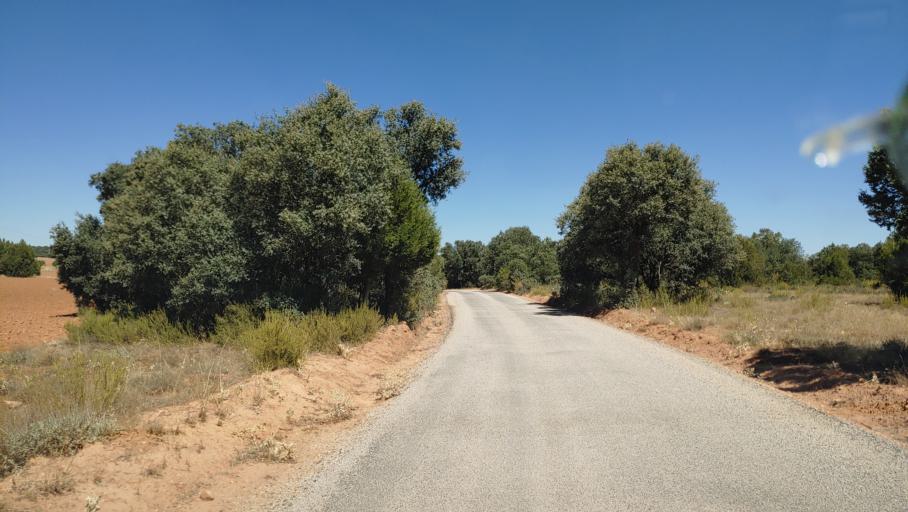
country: ES
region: Castille-La Mancha
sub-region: Provincia de Albacete
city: Ossa de Montiel
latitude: 38.9230
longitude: -2.7908
